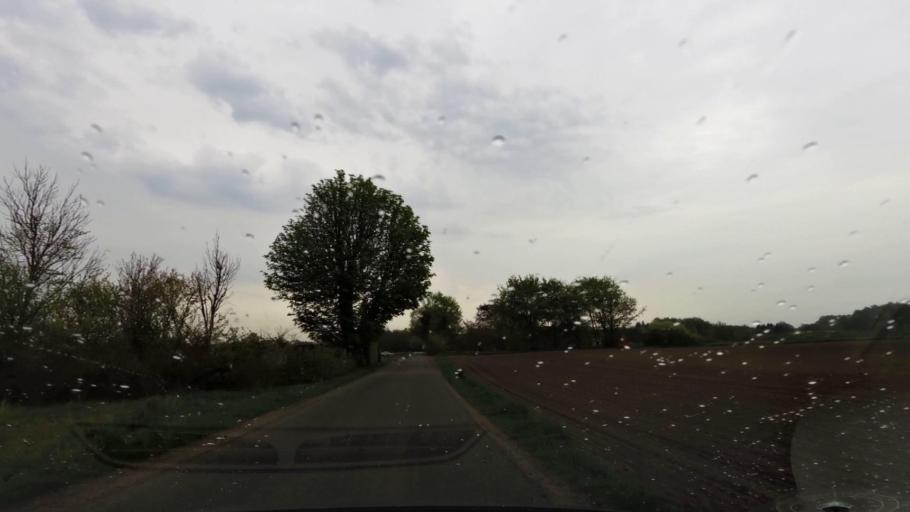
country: DK
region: South Denmark
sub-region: Faaborg-Midtfyn Kommune
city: Ringe
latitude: 55.1878
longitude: 10.5702
